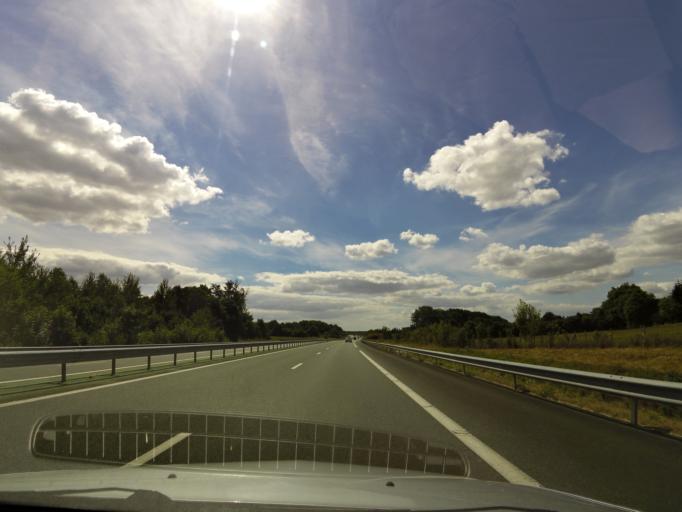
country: FR
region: Pays de la Loire
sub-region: Departement de la Vendee
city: La Ferriere
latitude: 46.6982
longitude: -1.2994
